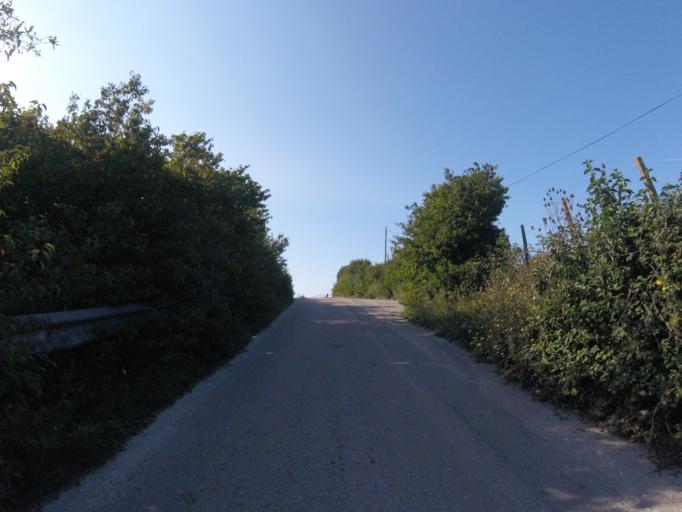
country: GB
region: England
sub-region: Brighton and Hove
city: Hove
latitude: 50.8698
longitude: -0.1498
